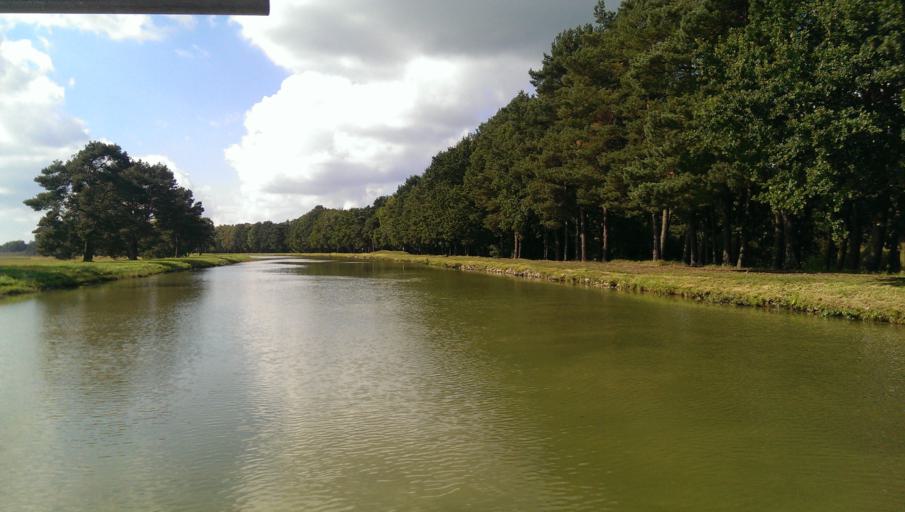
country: DE
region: Brandenburg
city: Melchow
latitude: 52.8612
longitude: 13.7014
